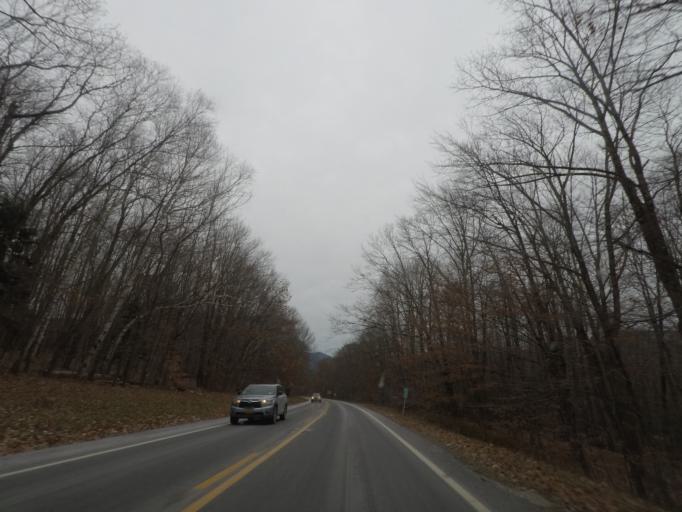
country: US
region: Massachusetts
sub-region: Berkshire County
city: Williamstown
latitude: 42.6954
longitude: -73.2385
